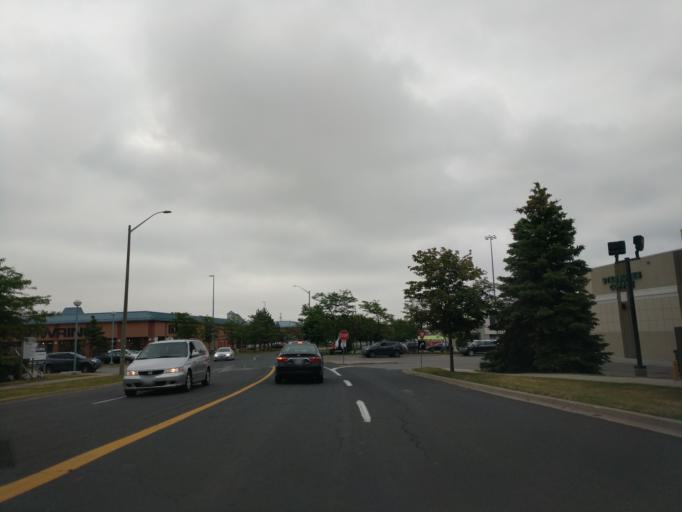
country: CA
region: Ontario
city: Markham
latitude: 43.8499
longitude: -79.3514
